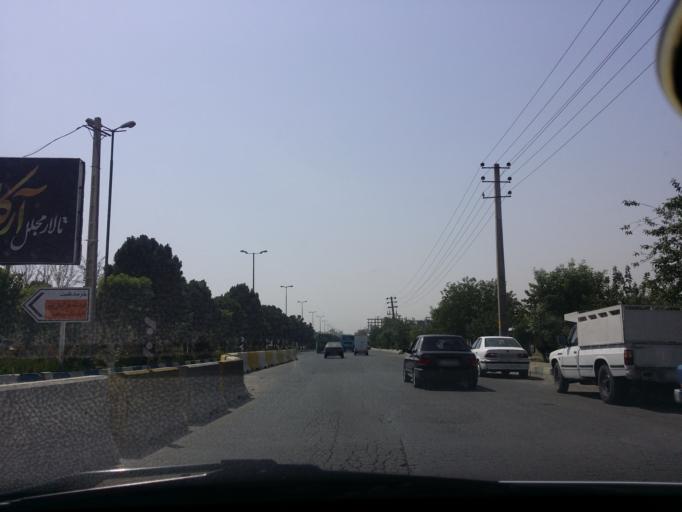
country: IR
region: Alborz
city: Karaj
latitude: 35.8542
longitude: 50.8990
